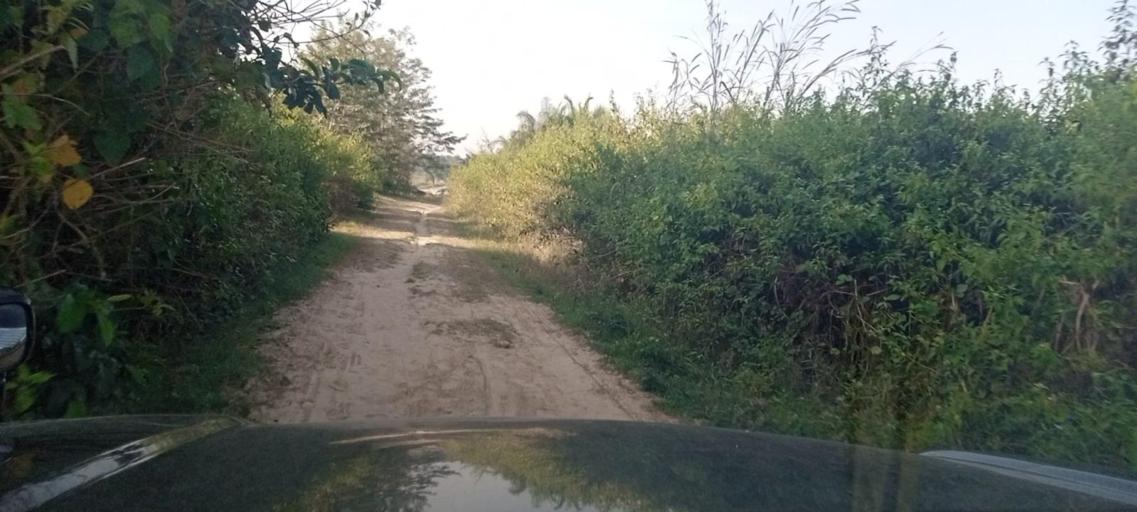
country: CD
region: Kasai-Oriental
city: Lubao
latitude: -5.4626
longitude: 25.6416
